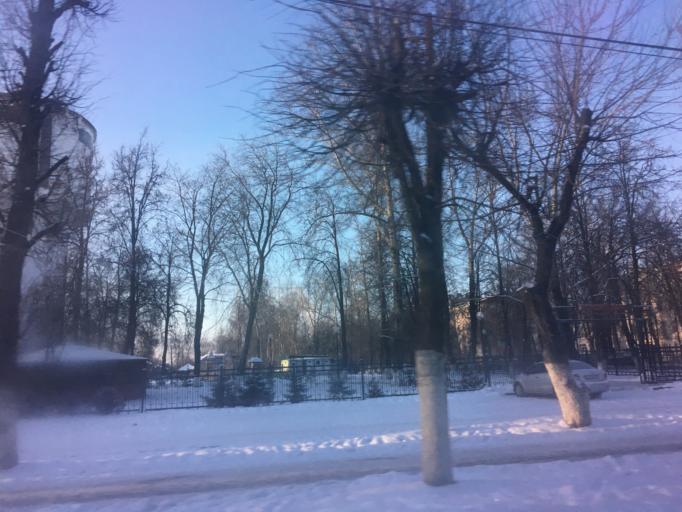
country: RU
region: Tula
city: Tula
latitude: 54.2124
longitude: 37.6664
